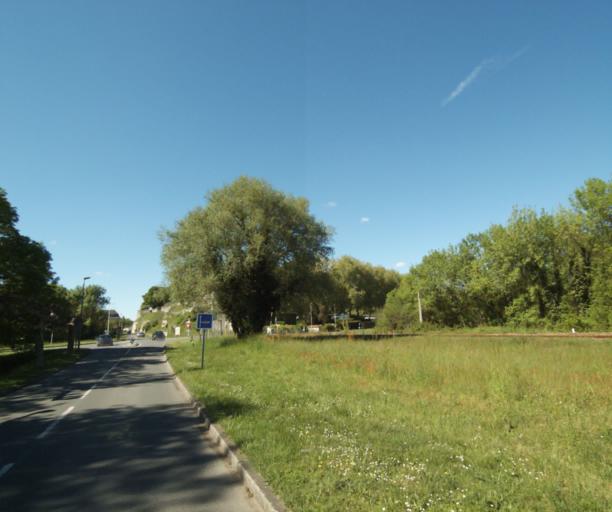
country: FR
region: Poitou-Charentes
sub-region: Departement de la Charente-Maritime
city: Bussac-sur-Charente
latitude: 45.8319
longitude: -0.6465
